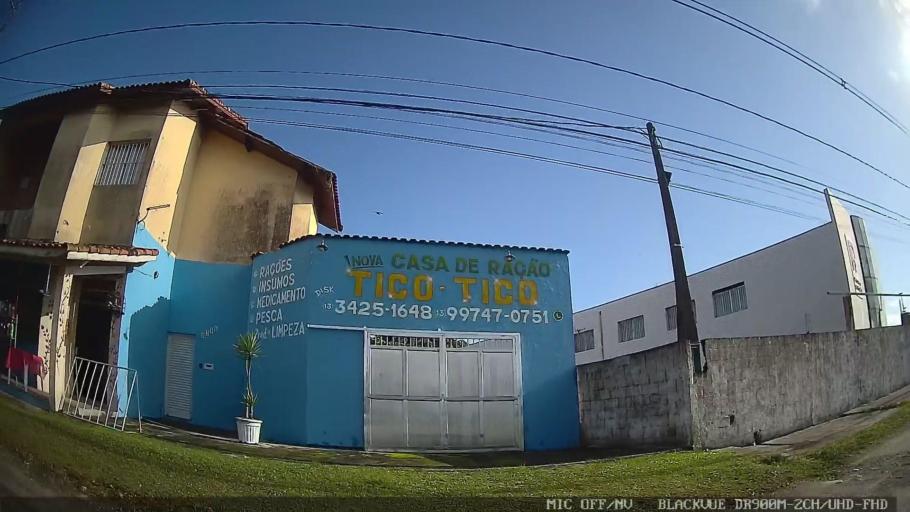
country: BR
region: Sao Paulo
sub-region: Itanhaem
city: Itanhaem
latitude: -24.2162
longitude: -46.8728
